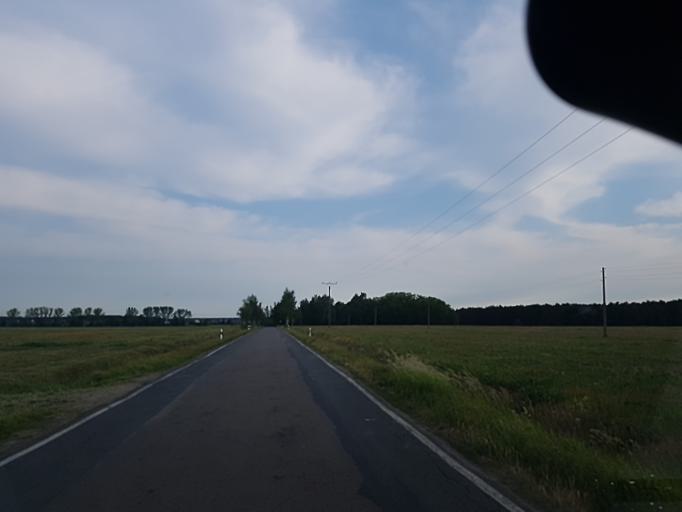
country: DE
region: Saxony-Anhalt
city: Jessen
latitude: 51.8123
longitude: 12.9523
